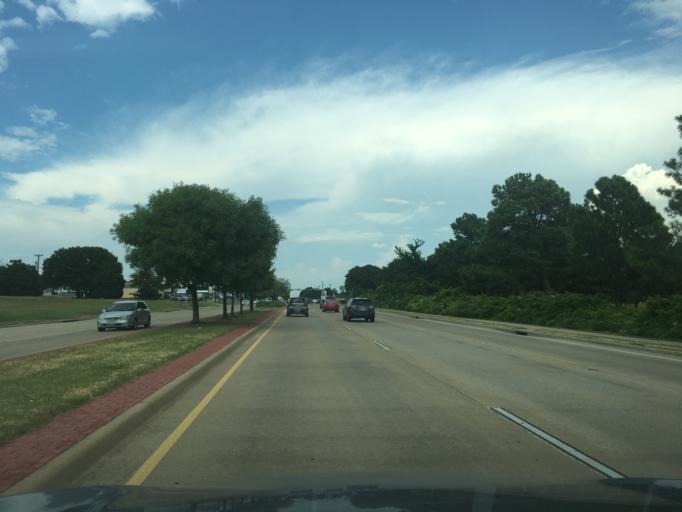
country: US
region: Texas
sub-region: Denton County
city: Denton
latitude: 33.2319
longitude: -97.1202
